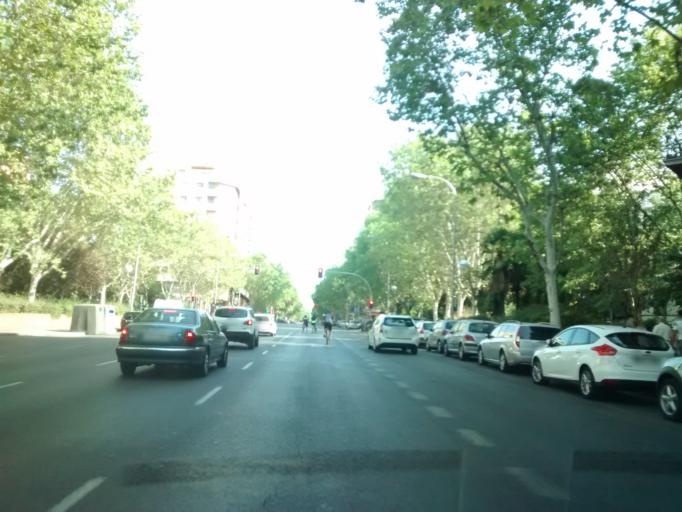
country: ES
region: Madrid
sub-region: Provincia de Madrid
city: Arganzuela
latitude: 40.4012
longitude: -3.6939
